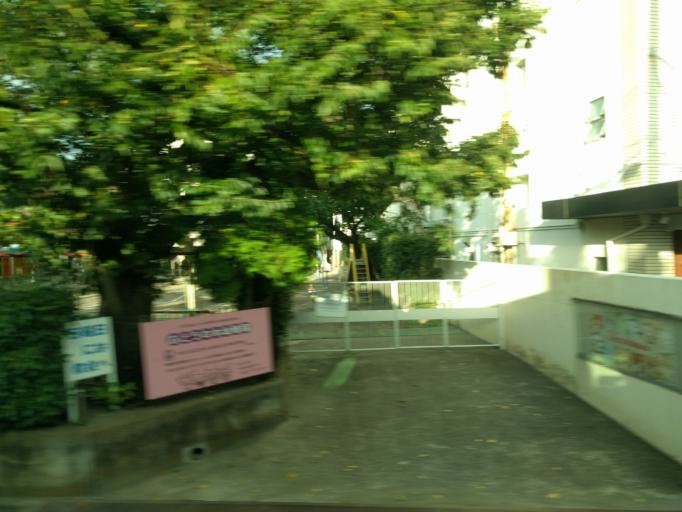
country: JP
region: Kanagawa
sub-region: Kawasaki-shi
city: Kawasaki
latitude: 35.5890
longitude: 139.6807
